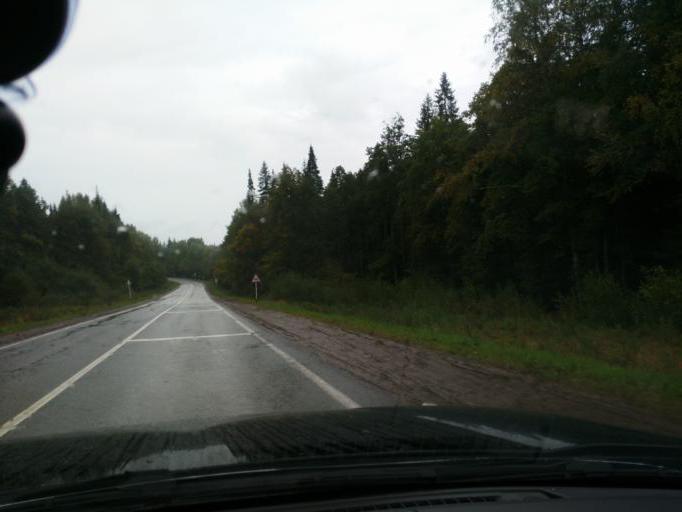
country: RU
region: Perm
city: Yugo-Kamskiy
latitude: 57.5019
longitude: 55.6883
